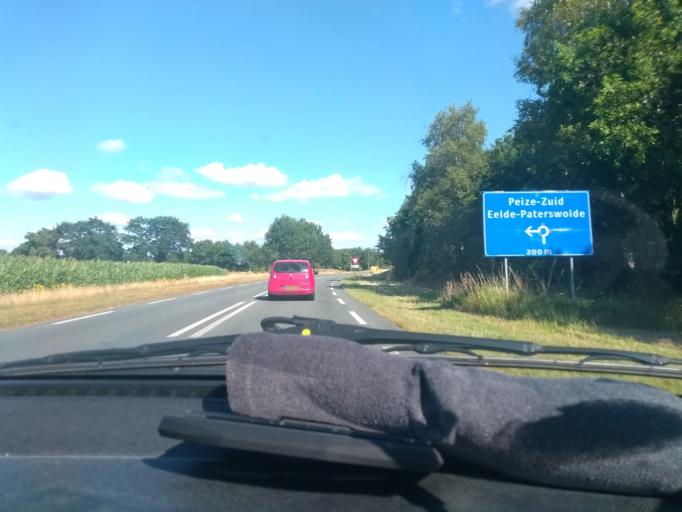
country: NL
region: Drenthe
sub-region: Gemeente Tynaarlo
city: Vries
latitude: 53.1388
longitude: 6.4931
